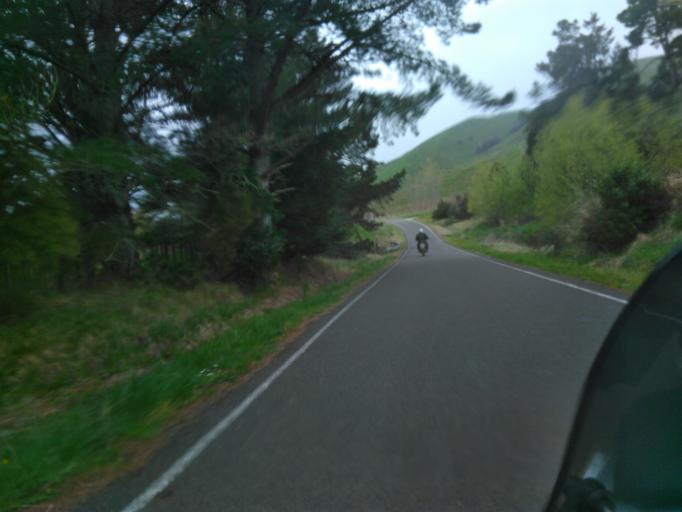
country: NZ
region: Gisborne
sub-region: Gisborne District
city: Gisborne
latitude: -38.6462
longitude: 177.7113
